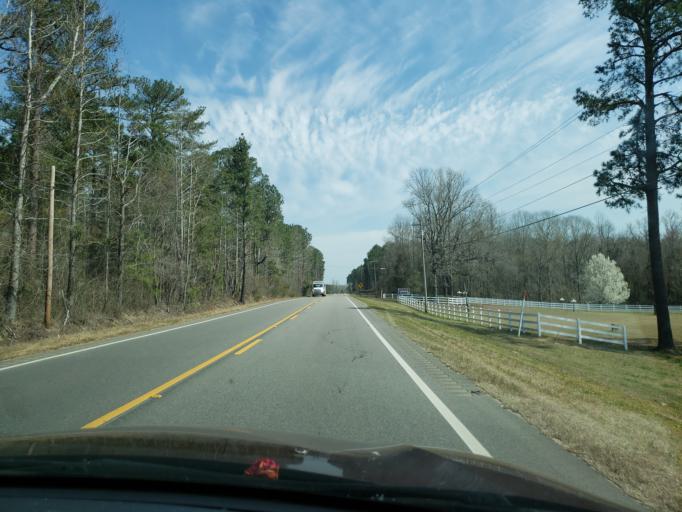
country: US
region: Alabama
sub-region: Elmore County
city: Eclectic
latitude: 32.5727
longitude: -86.1078
